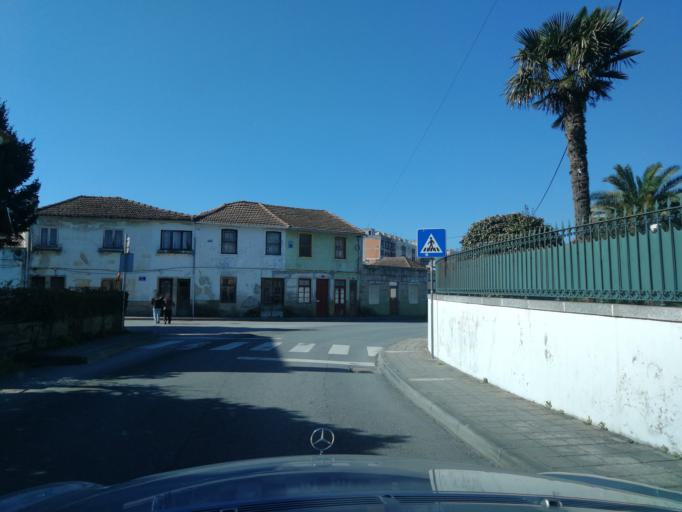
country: PT
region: Braga
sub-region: Vila Nova de Famalicao
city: Calendario
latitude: 41.4011
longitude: -8.5277
